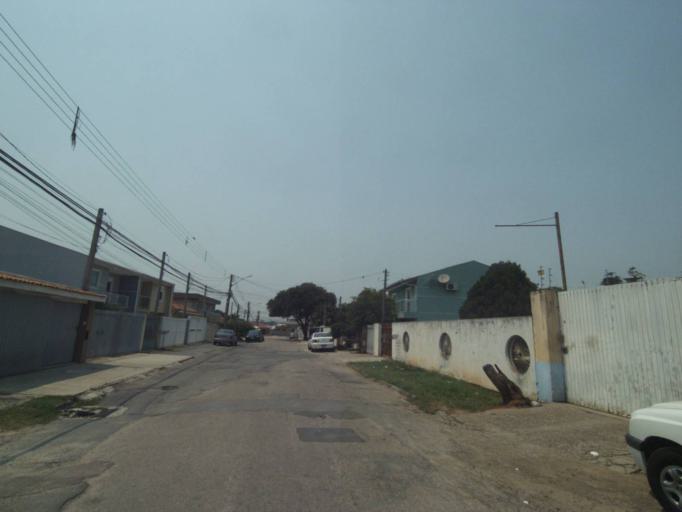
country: BR
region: Parana
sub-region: Sao Jose Dos Pinhais
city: Sao Jose dos Pinhais
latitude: -25.5289
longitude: -49.2402
